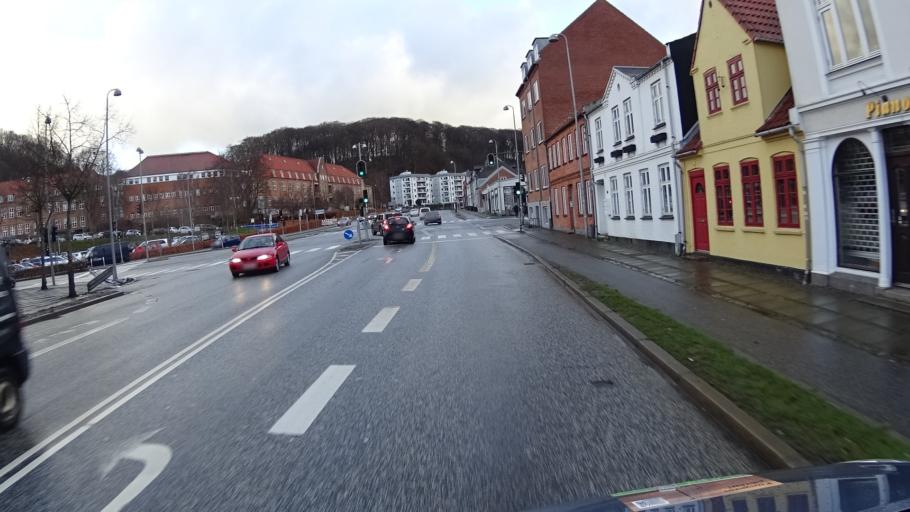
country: DK
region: South Denmark
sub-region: Vejle Kommune
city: Vejle
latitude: 55.7127
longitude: 9.5413
